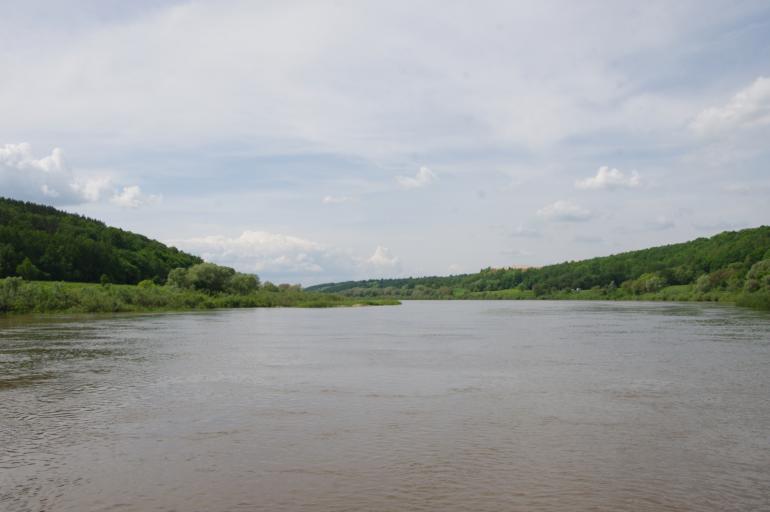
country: RU
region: Kaluga
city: Ferzikovo
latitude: 54.4457
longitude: 36.7967
